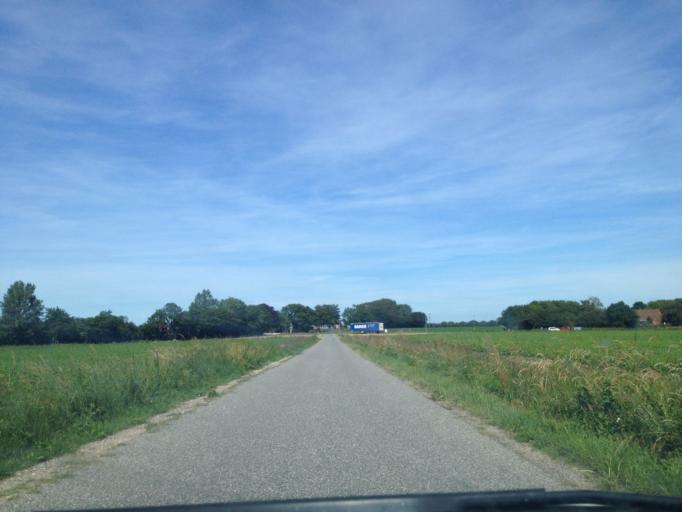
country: DK
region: Central Jutland
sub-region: Samso Kommune
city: Tranebjerg
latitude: 55.9561
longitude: 10.5522
